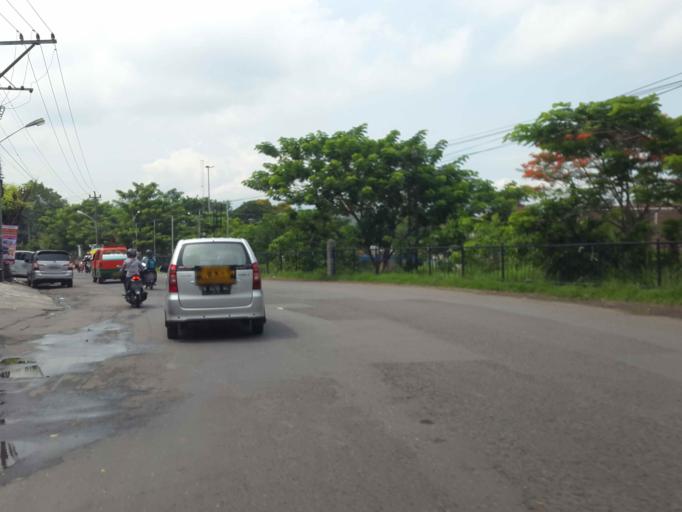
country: ID
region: Central Java
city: Semarang
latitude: -7.0072
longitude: 110.3962
